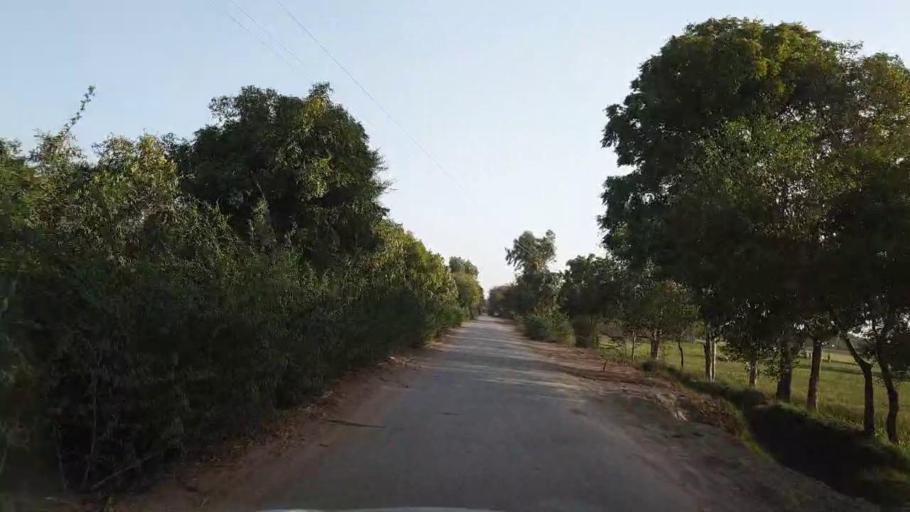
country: PK
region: Sindh
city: Tando Ghulam Ali
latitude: 25.1235
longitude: 68.9069
